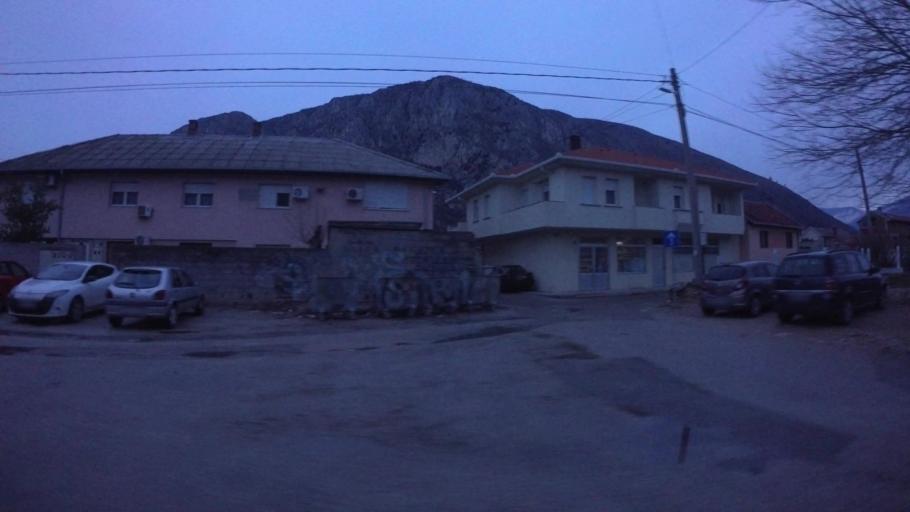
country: BA
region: Federation of Bosnia and Herzegovina
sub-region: Hercegovacko-Bosanski Kanton
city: Mostar
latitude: 43.3292
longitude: 17.8196
